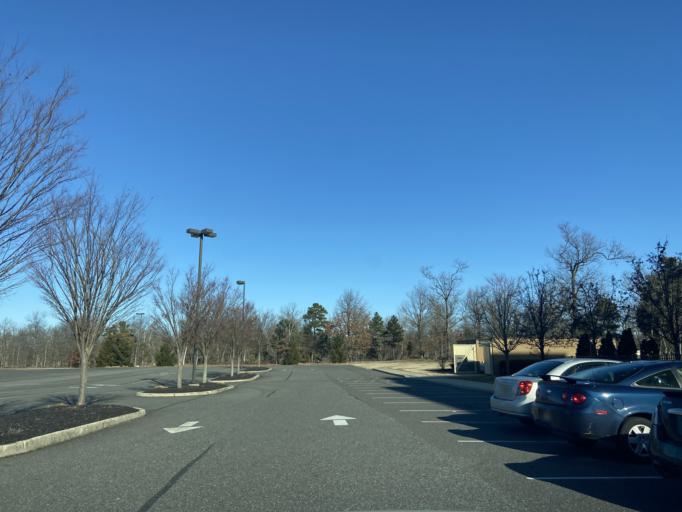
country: US
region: New Jersey
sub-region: Cumberland County
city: Vineland
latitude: 39.4899
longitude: -75.0660
